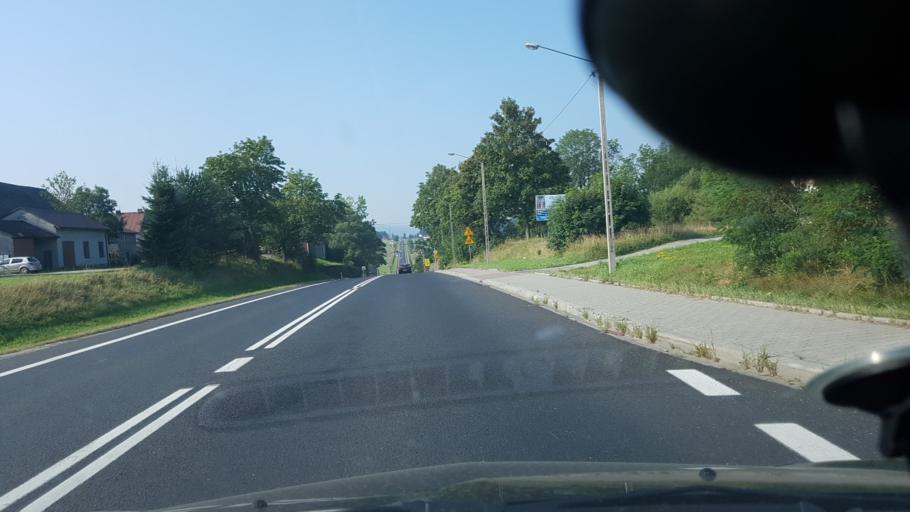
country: PL
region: Lesser Poland Voivodeship
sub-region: Powiat nowotarski
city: Chyzne
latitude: 49.4273
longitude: 19.6750
